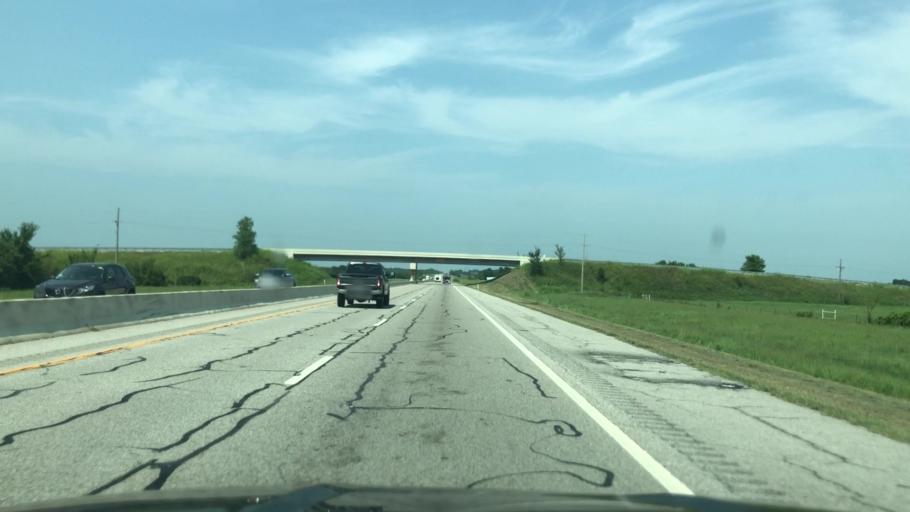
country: US
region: Oklahoma
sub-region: Ottawa County
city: Fairland
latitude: 36.7993
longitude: -94.8810
